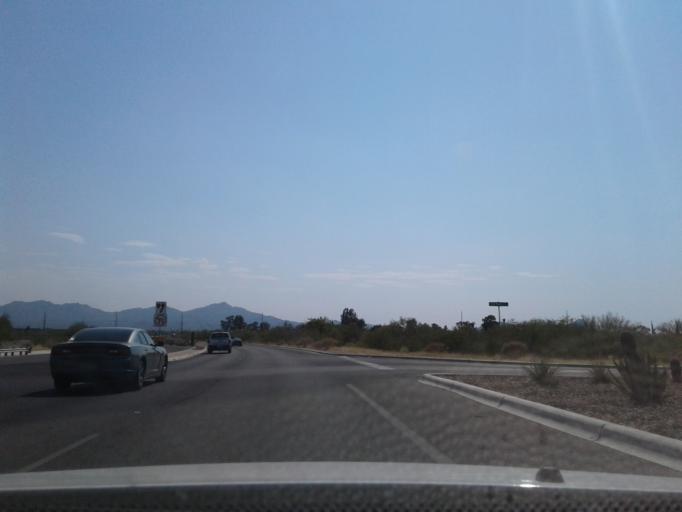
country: US
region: Arizona
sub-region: Pima County
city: Casas Adobes
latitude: 32.3514
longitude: -111.0080
